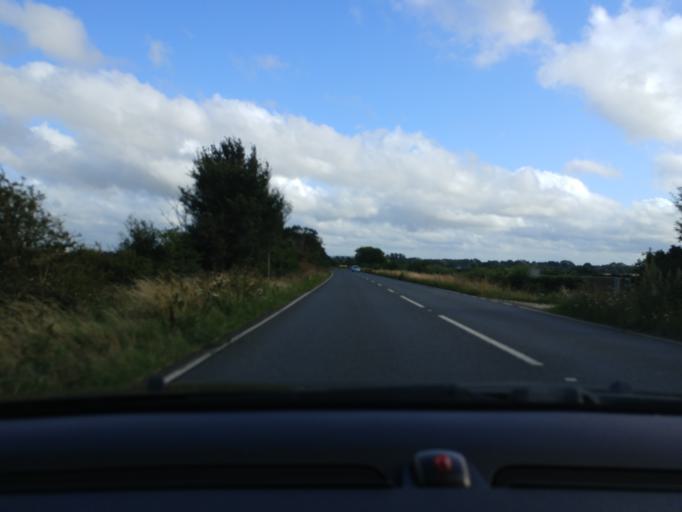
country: GB
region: England
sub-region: Oxfordshire
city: Kidlington
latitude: 51.8759
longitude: -1.2300
